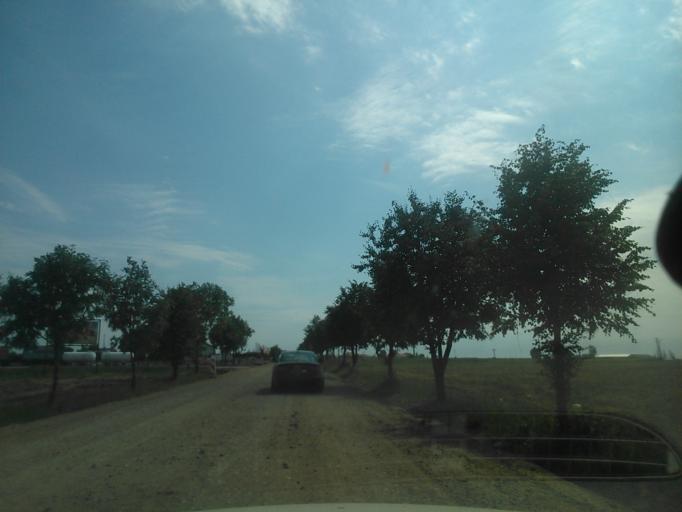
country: PL
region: Warmian-Masurian Voivodeship
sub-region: Powiat dzialdowski
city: Dzialdowo
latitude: 53.2243
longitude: 20.2026
